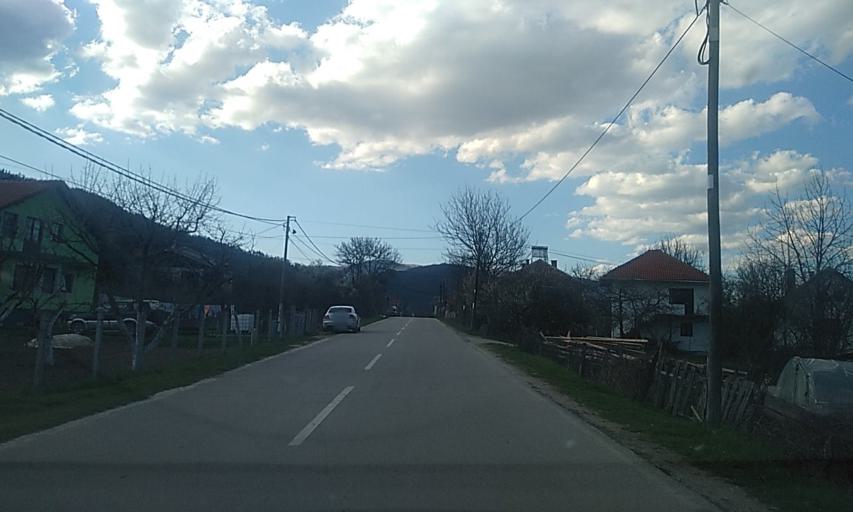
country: RS
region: Central Serbia
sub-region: Pcinjski Okrug
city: Bosilegrad
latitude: 42.4794
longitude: 22.4776
